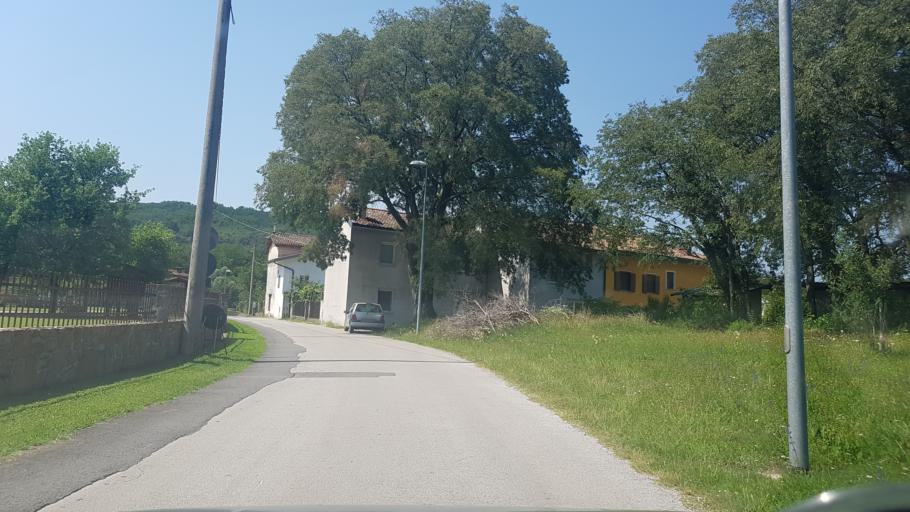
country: IT
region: Friuli Venezia Giulia
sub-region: Provincia di Gorizia
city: Savogna d'Isonzo
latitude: 45.9022
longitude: 13.5696
